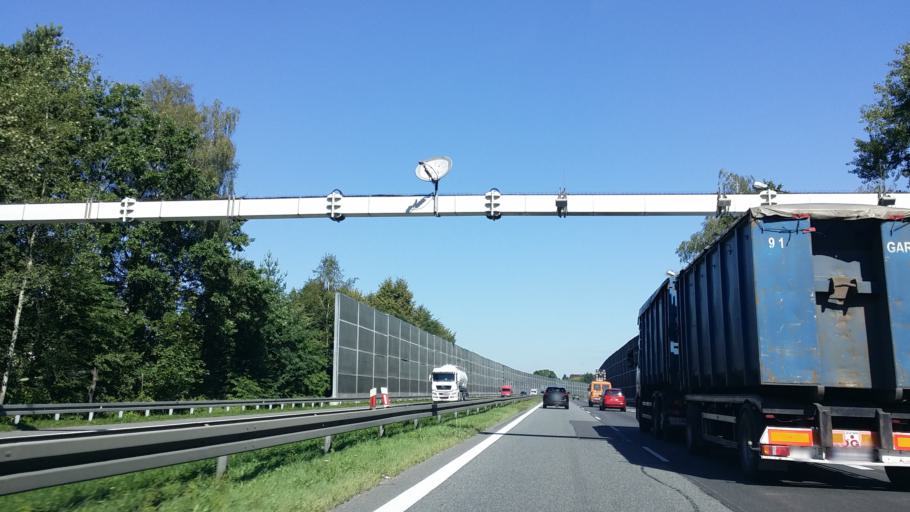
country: PL
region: Silesian Voivodeship
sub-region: Myslowice
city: Myslowice
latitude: 50.1850
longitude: 19.1669
